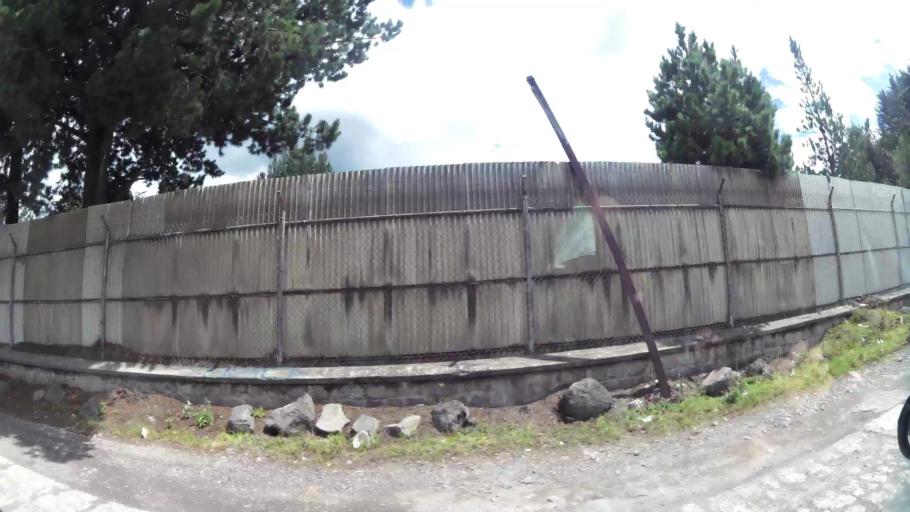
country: EC
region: Pichincha
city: Sangolqui
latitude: -0.3463
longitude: -78.5451
